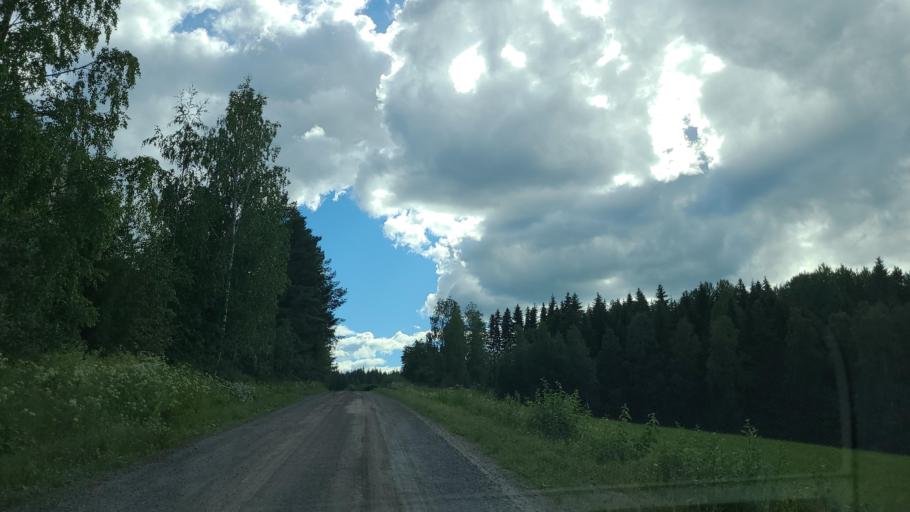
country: FI
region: Central Finland
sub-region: Jaemsae
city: Jaemsae
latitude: 61.9330
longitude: 25.3298
